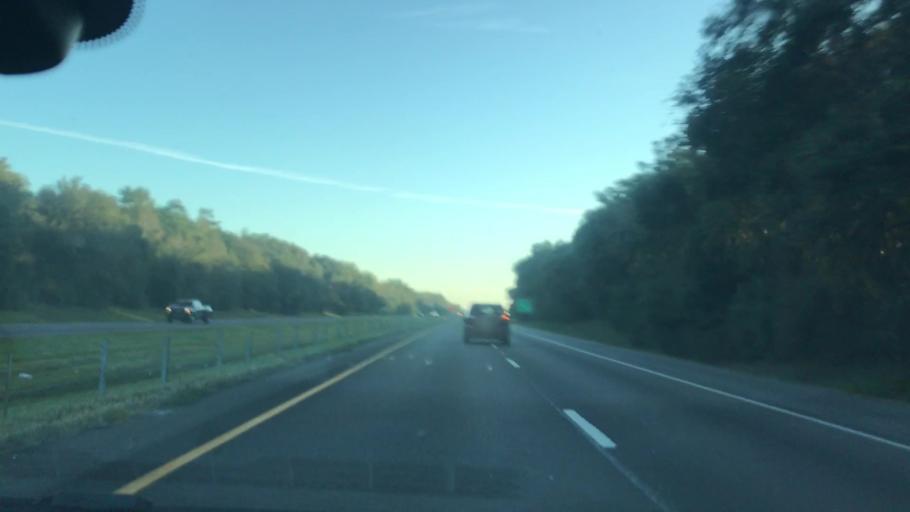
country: US
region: Alabama
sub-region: Mobile County
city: Theodore
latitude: 30.5288
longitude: -88.2564
